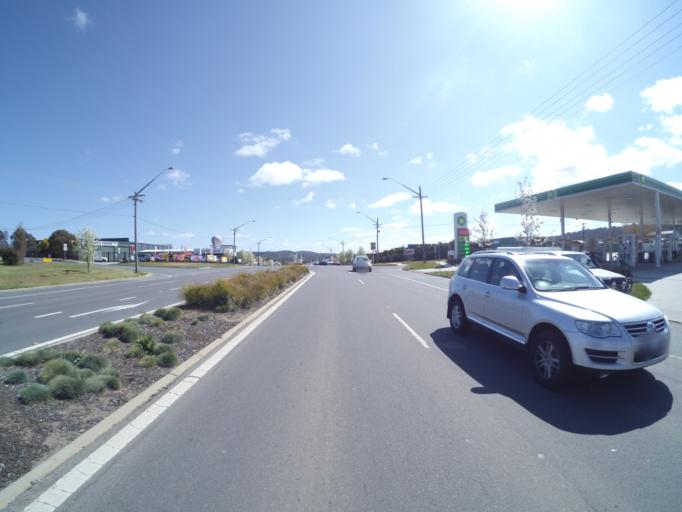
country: AU
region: New South Wales
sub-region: Queanbeyan
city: Queanbeyan
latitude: -35.3415
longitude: 149.2442
